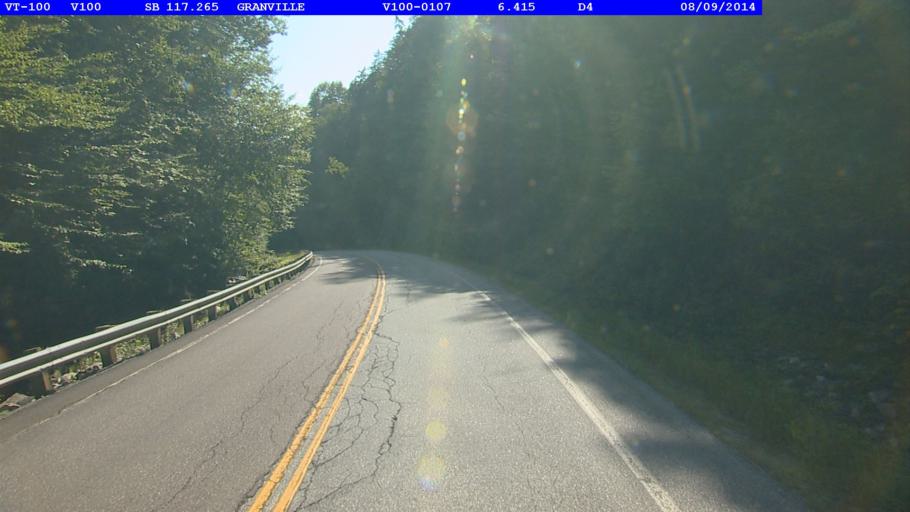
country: US
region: Vermont
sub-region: Orange County
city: Randolph
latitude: 44.0239
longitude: -72.8363
